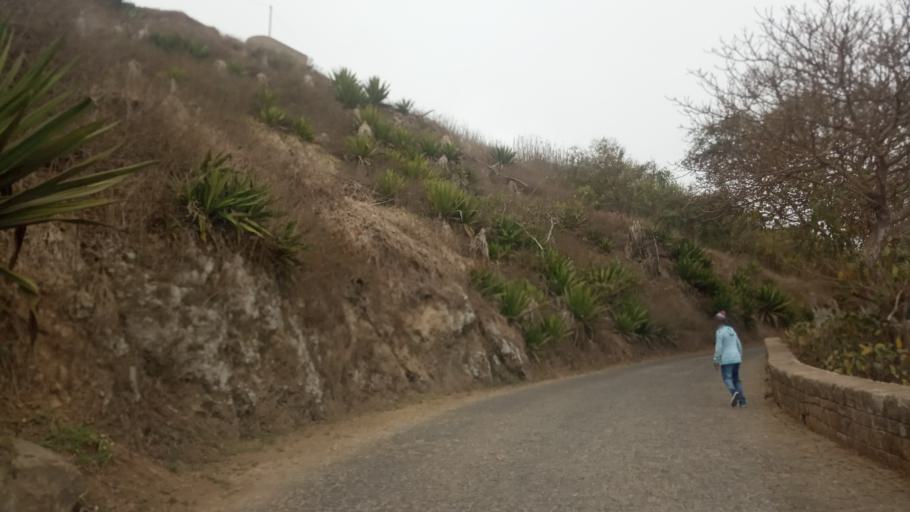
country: CV
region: Brava
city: Vila Nova Sintra
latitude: 14.8718
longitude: -24.6998
